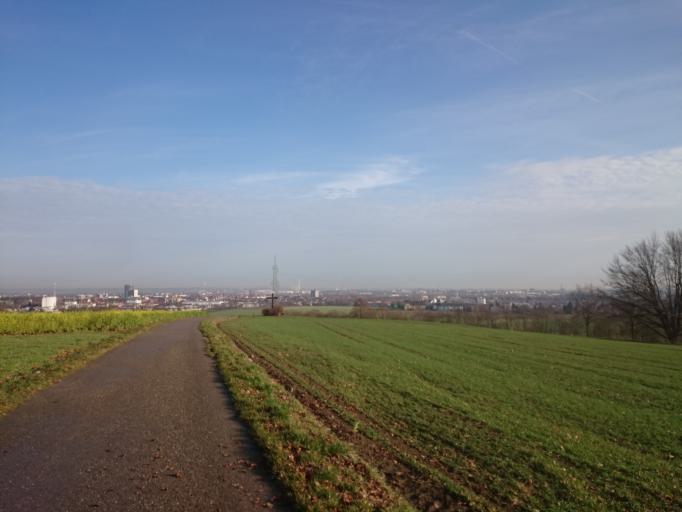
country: DE
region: Bavaria
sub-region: Swabia
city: Stadtbergen
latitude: 48.3722
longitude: 10.8305
